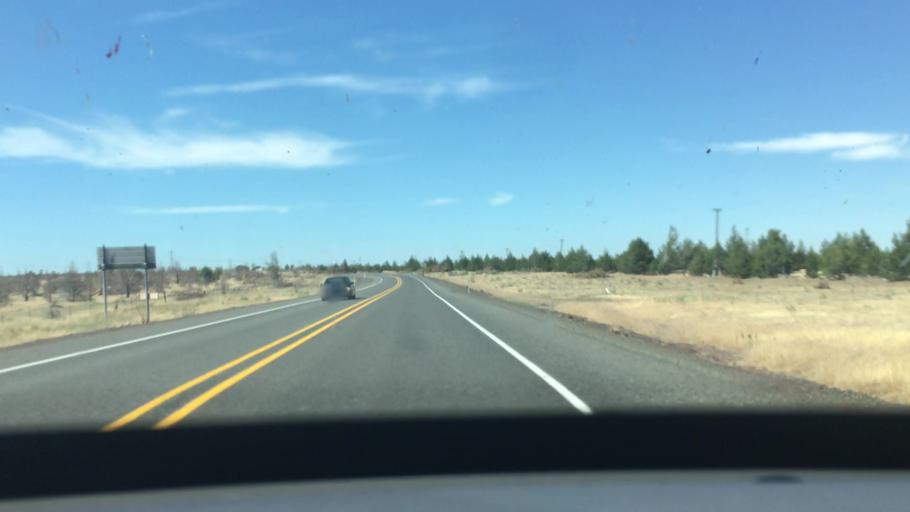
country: US
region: Oregon
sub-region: Jefferson County
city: Madras
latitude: 44.9098
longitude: -120.9398
